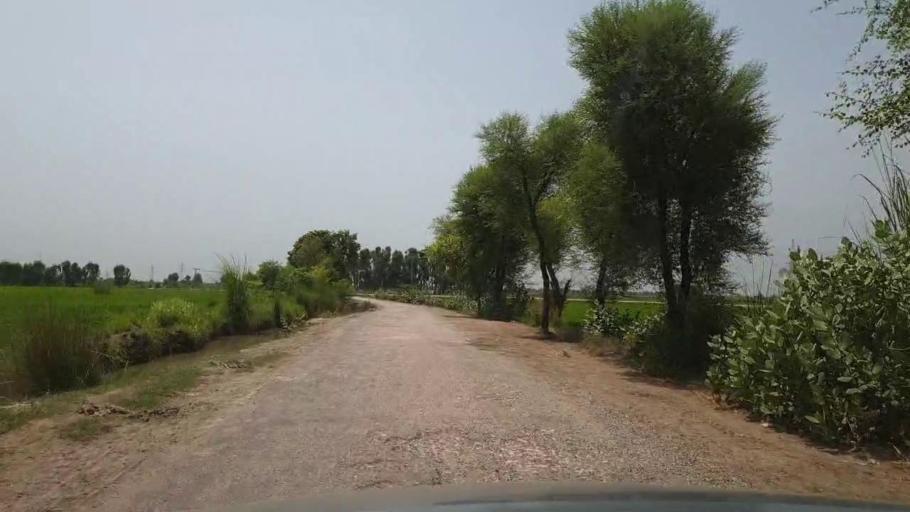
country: PK
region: Sindh
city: Madeji
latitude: 27.7745
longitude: 68.4321
